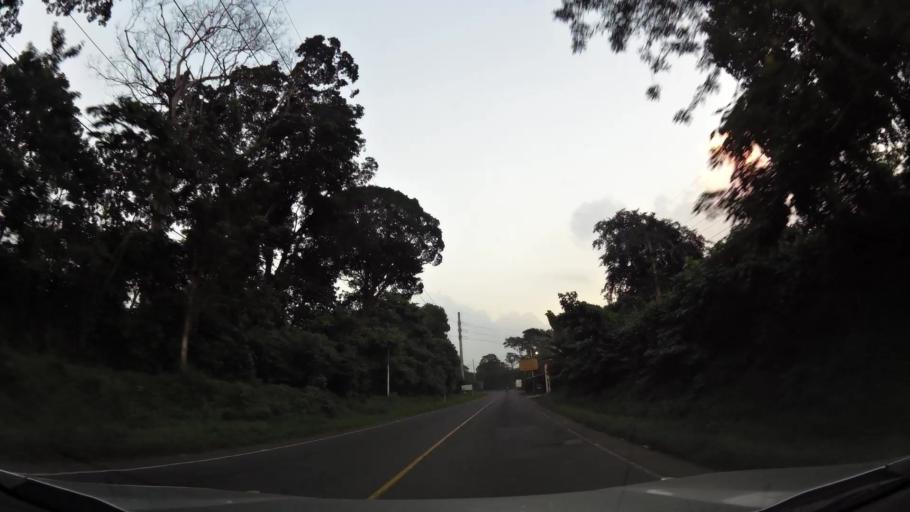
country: GT
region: Retalhuleu
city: San Martin Zapotitlan
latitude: 14.6017
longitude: -91.6110
